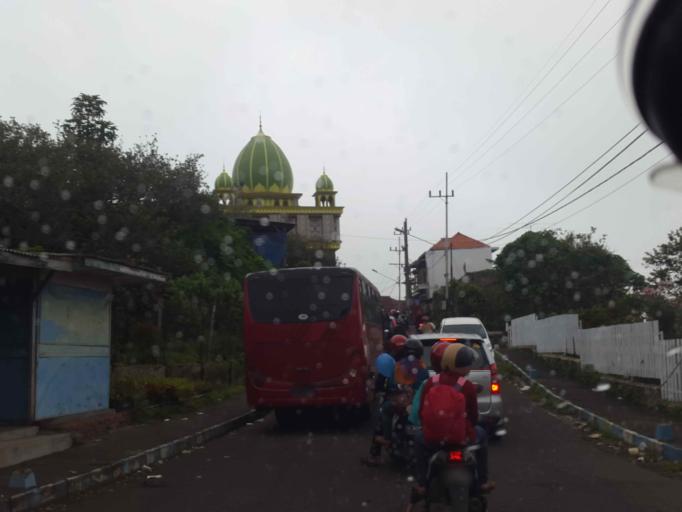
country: ID
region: East Java
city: Batu
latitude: -7.8242
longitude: 112.5290
